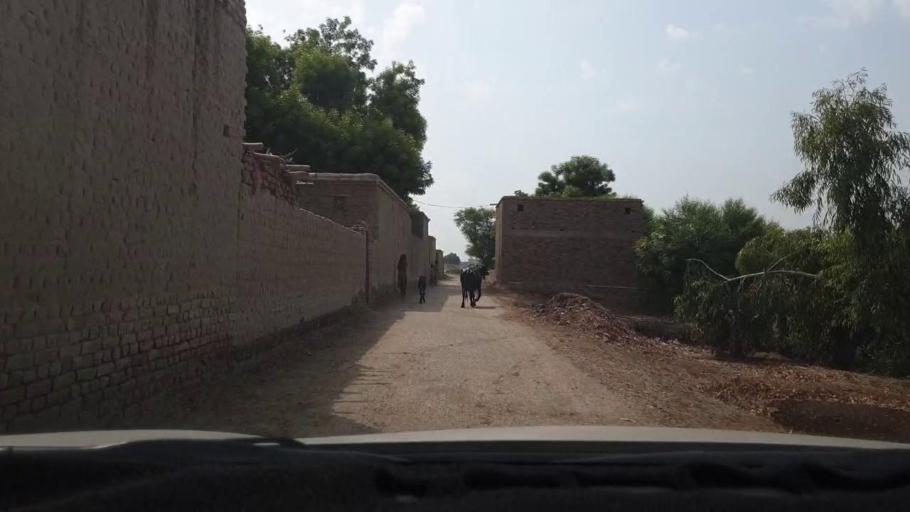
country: PK
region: Sindh
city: Dokri
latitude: 27.3869
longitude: 68.1227
